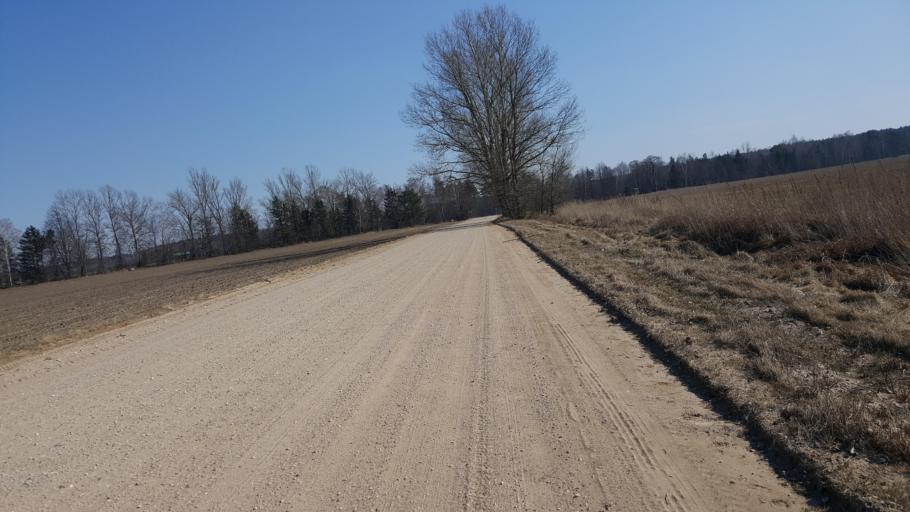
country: BY
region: Brest
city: Kamyanyets
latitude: 52.3560
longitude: 23.7722
